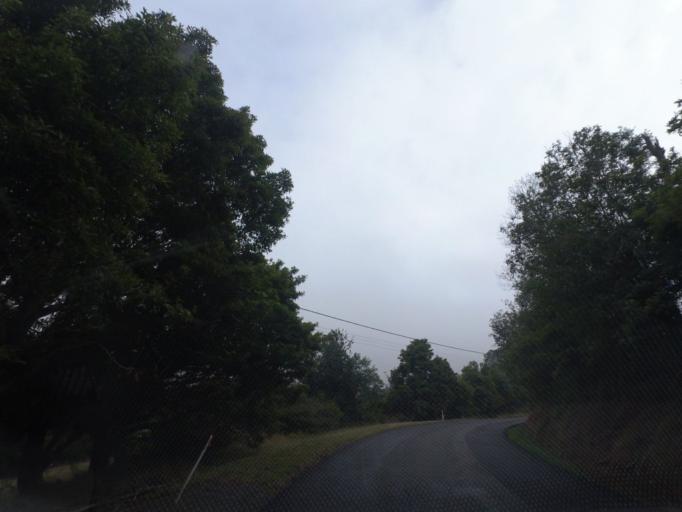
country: AU
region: Victoria
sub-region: Yarra Ranges
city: Yarra Junction
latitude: -37.7322
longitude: 145.5929
